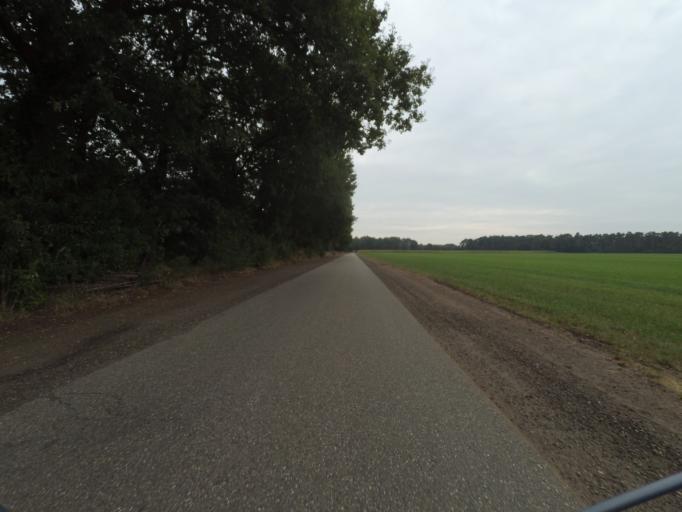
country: NL
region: Overijssel
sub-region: Gemeente Losser
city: Losser
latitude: 52.2791
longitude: 7.0443
